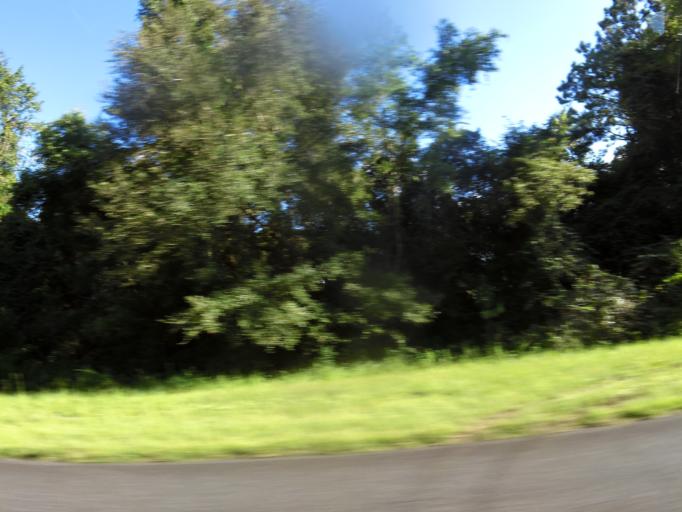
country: US
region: Florida
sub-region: Wakulla County
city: Crawfordville
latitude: 30.0643
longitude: -84.5122
